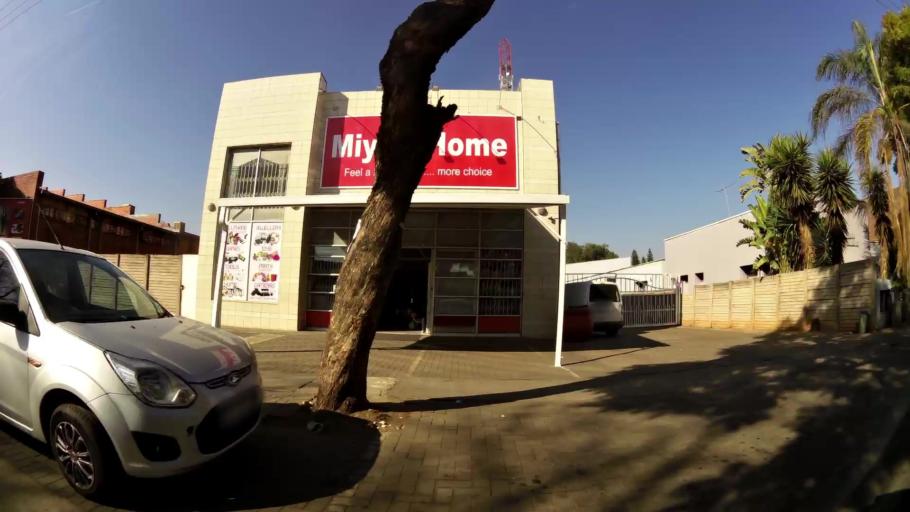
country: ZA
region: Gauteng
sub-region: City of Tshwane Metropolitan Municipality
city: Pretoria
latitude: -25.6751
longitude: 28.1727
